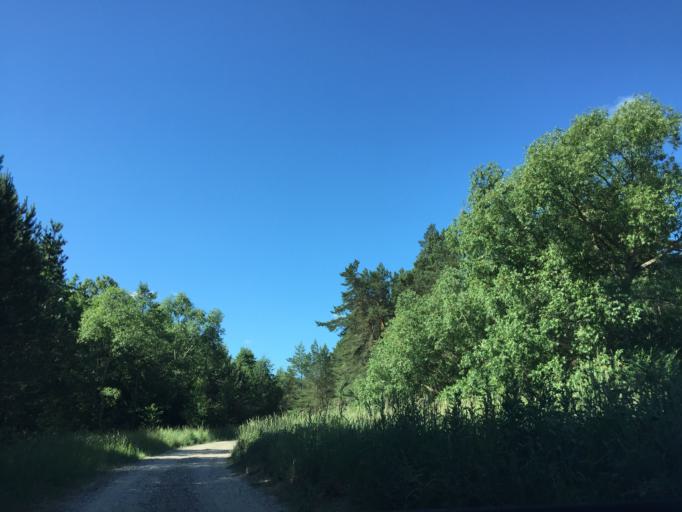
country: LV
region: Ventspils
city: Ventspils
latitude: 57.4560
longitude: 21.6323
